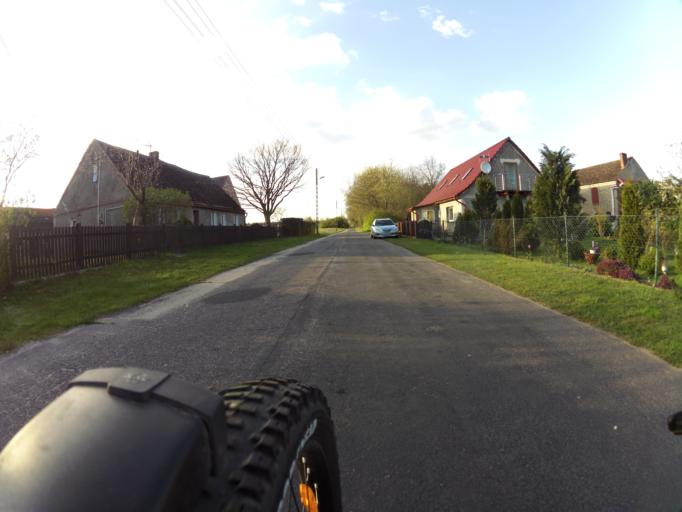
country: PL
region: West Pomeranian Voivodeship
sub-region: Powiat gryficki
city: Ploty
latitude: 53.7443
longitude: 15.2720
